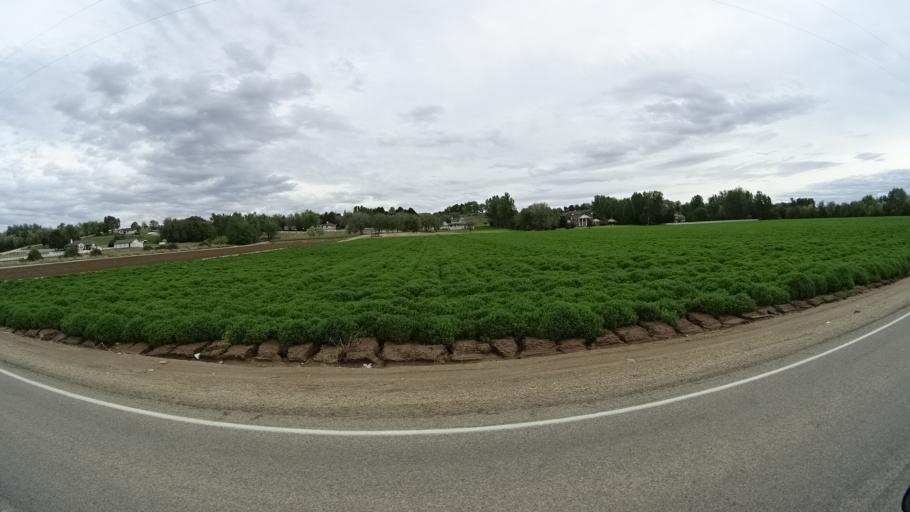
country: US
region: Idaho
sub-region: Ada County
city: Star
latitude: 43.7173
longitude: -116.5089
